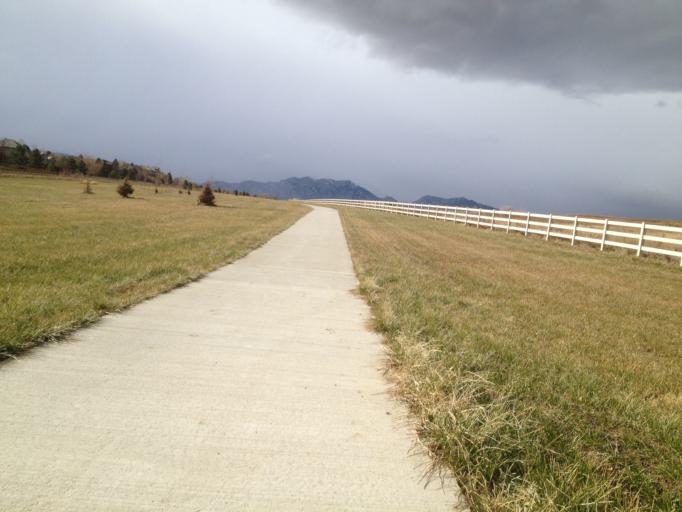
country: US
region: Colorado
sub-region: Boulder County
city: Superior
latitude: 39.9474
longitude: -105.1537
